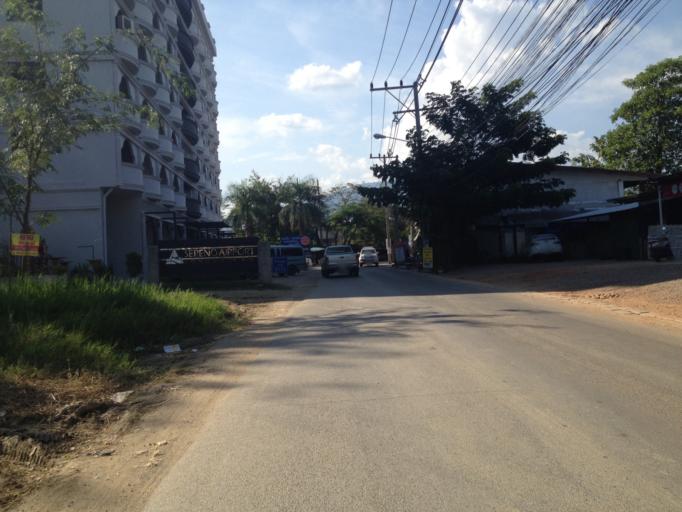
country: TH
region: Chiang Mai
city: Chiang Mai
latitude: 18.7638
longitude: 98.9770
